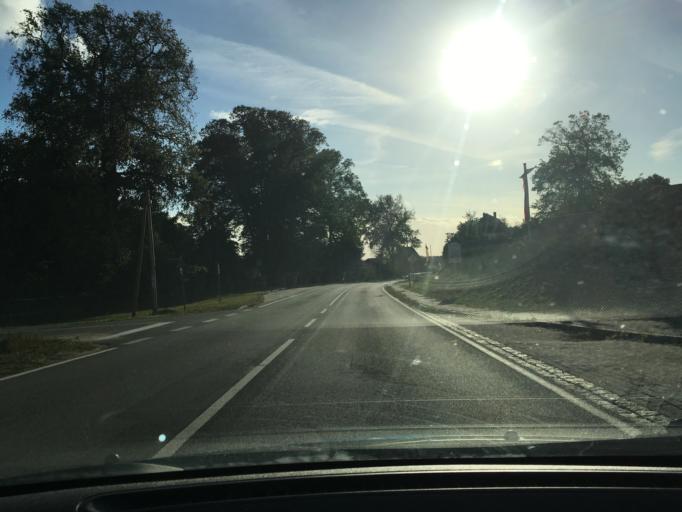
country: DE
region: Lower Saxony
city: Neu Darchau
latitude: 53.3818
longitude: 10.8923
